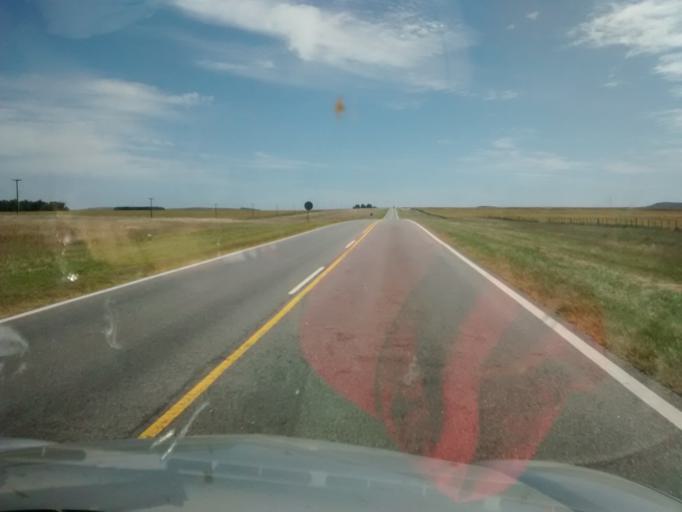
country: AR
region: Buenos Aires
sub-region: Partido de Balcarce
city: Balcarce
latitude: -37.6480
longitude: -58.5768
